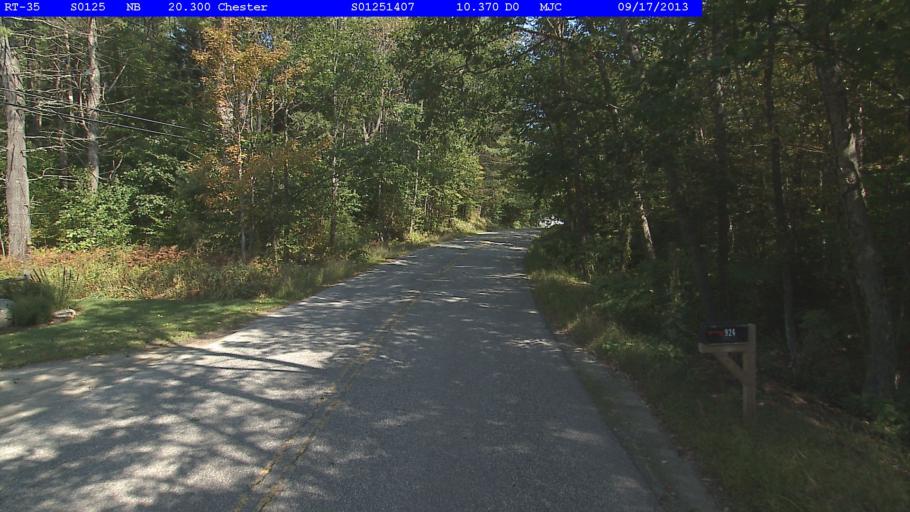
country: US
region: Vermont
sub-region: Windsor County
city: Chester
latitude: 43.2528
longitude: -72.6038
